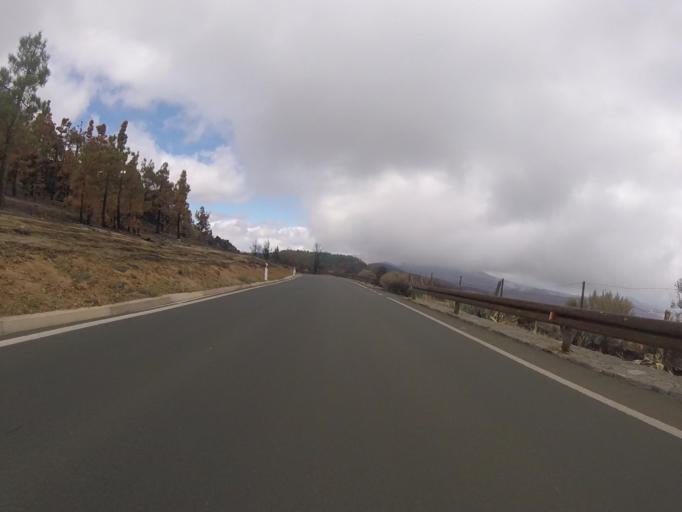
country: ES
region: Canary Islands
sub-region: Provincia de Las Palmas
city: San Bartolome
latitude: 27.9697
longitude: -15.5689
